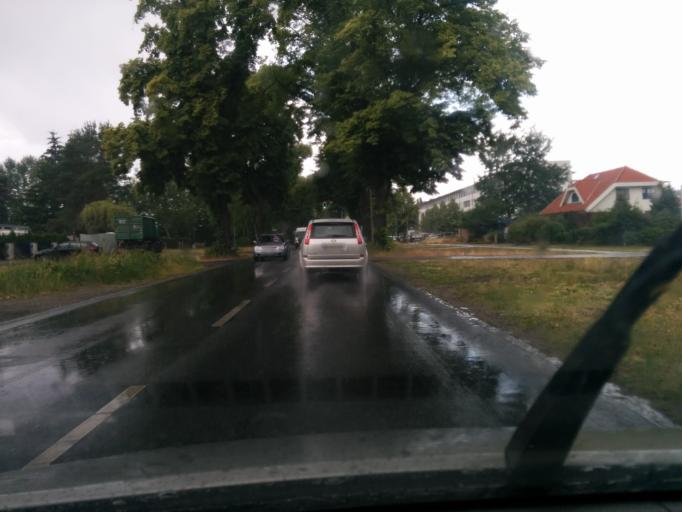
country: DE
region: Berlin
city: Staaken
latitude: 52.5563
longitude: 13.1417
